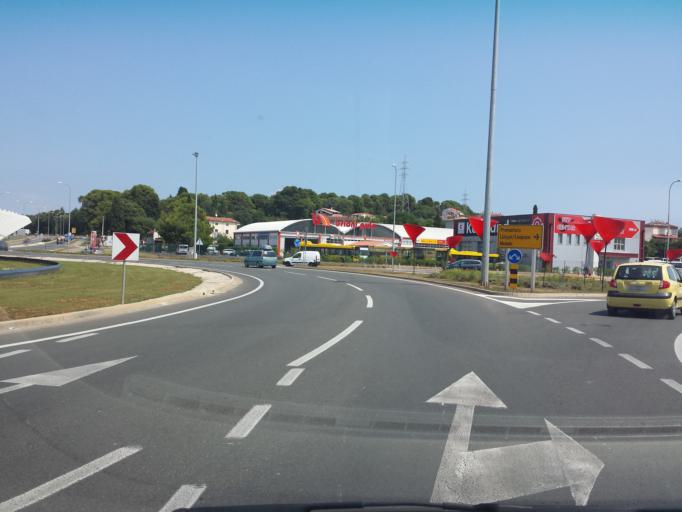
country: HR
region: Istarska
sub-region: Grad Pula
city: Pula
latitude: 44.8801
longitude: 13.8642
